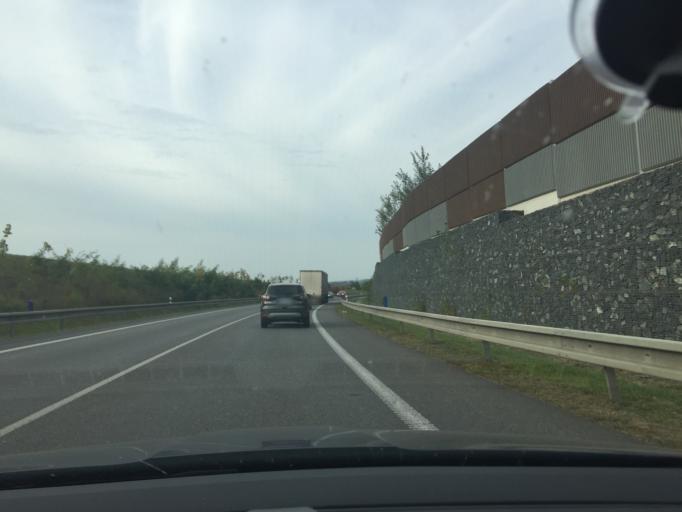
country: CZ
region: Central Bohemia
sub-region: Okres Kolin
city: Kolin
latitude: 50.0254
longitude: 15.1693
